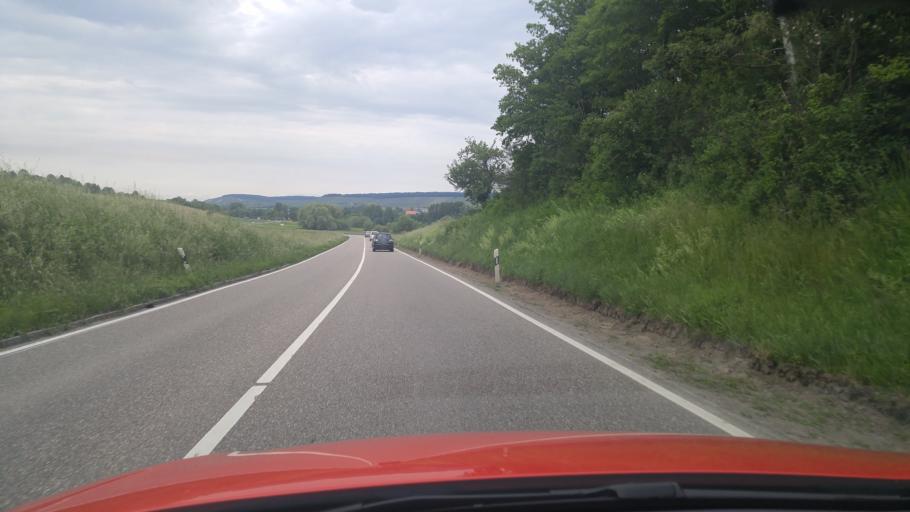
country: DE
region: Baden-Wuerttemberg
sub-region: Regierungsbezirk Stuttgart
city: Lehrensteinsfeld
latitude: 49.1385
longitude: 9.3517
